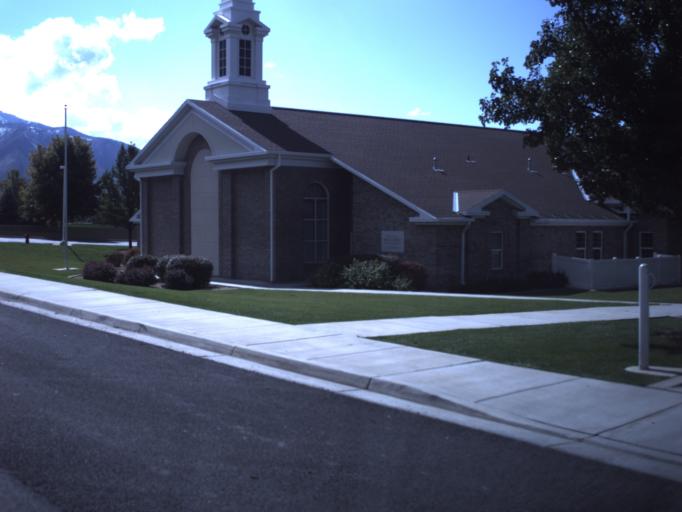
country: US
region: Utah
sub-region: Utah County
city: Mapleton
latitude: 40.1189
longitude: -111.5787
